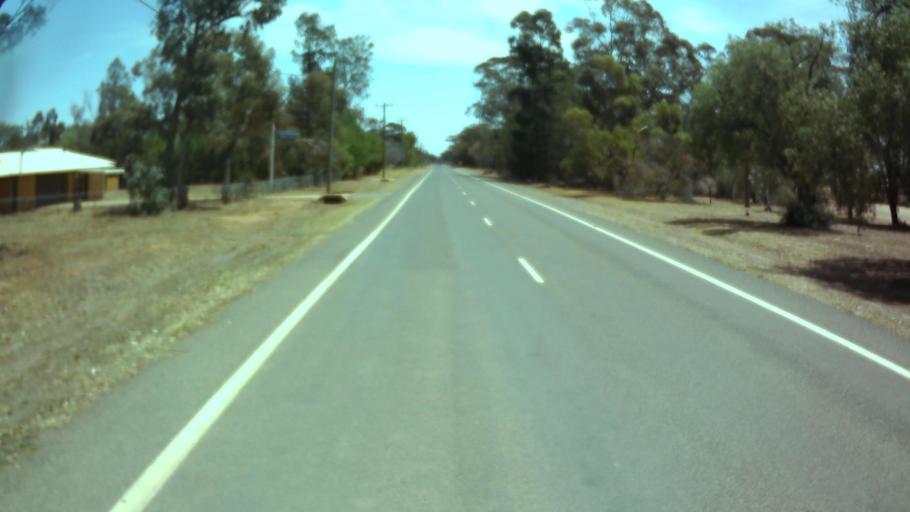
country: AU
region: New South Wales
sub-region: Weddin
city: Grenfell
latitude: -33.8438
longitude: 147.7388
